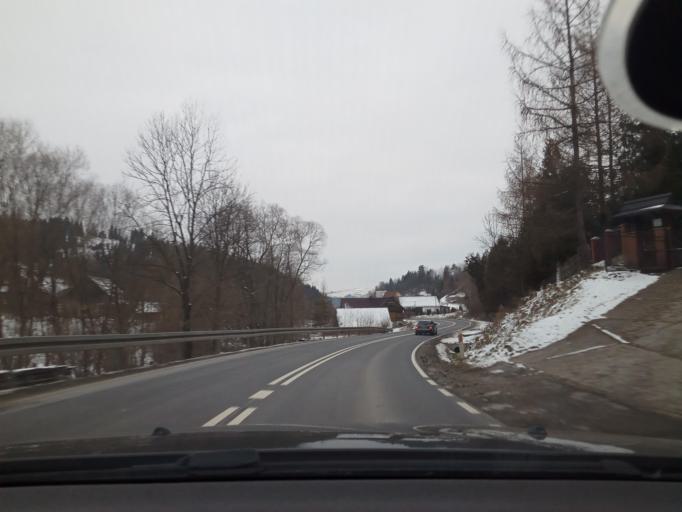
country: PL
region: Lesser Poland Voivodeship
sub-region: Powiat limanowski
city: Lubomierz
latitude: 49.6178
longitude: 20.1715
